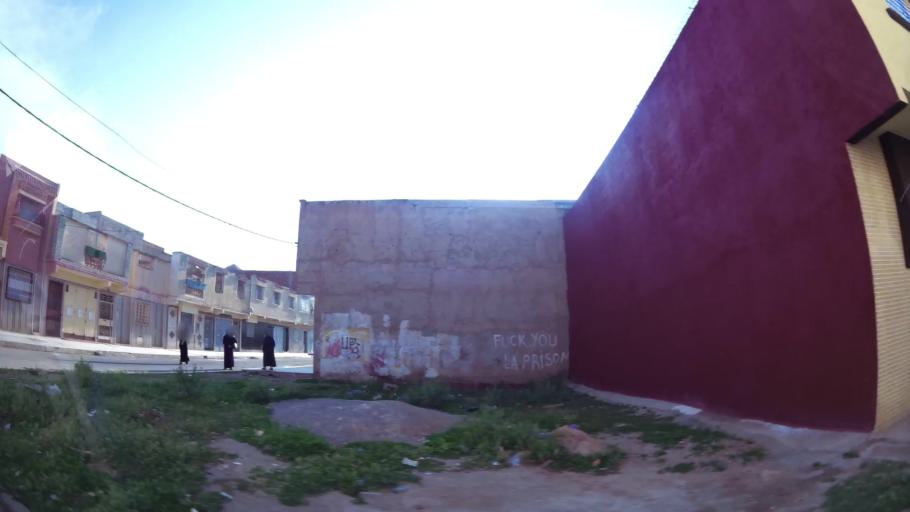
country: MA
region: Oriental
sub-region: Oujda-Angad
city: Oujda
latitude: 34.7066
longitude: -1.9012
